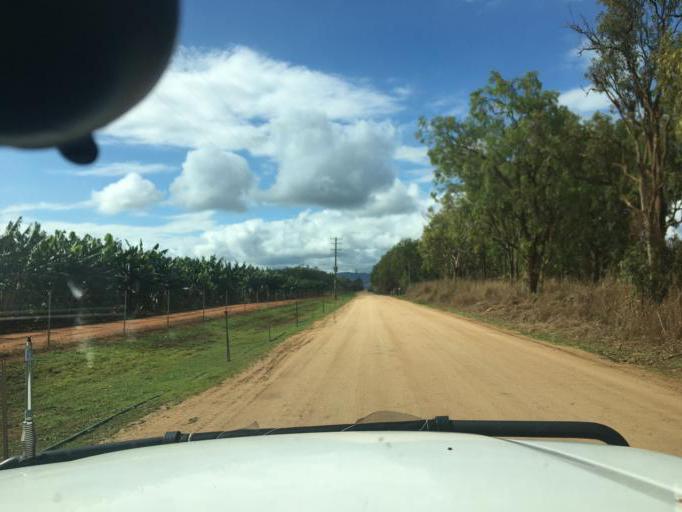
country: AU
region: Queensland
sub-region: Tablelands
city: Mareeba
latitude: -17.0961
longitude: 145.4121
